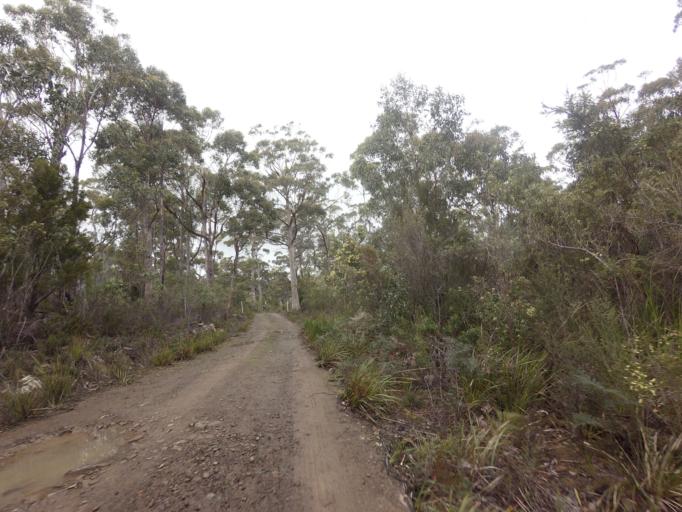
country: AU
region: Tasmania
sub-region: Huon Valley
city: Geeveston
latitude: -43.4585
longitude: 146.9103
